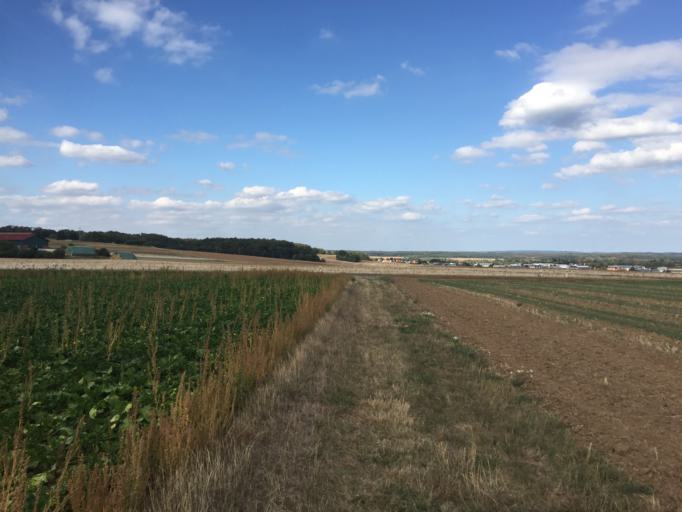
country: DE
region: Hesse
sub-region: Regierungsbezirk Giessen
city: Lich
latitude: 50.4952
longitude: 8.8215
